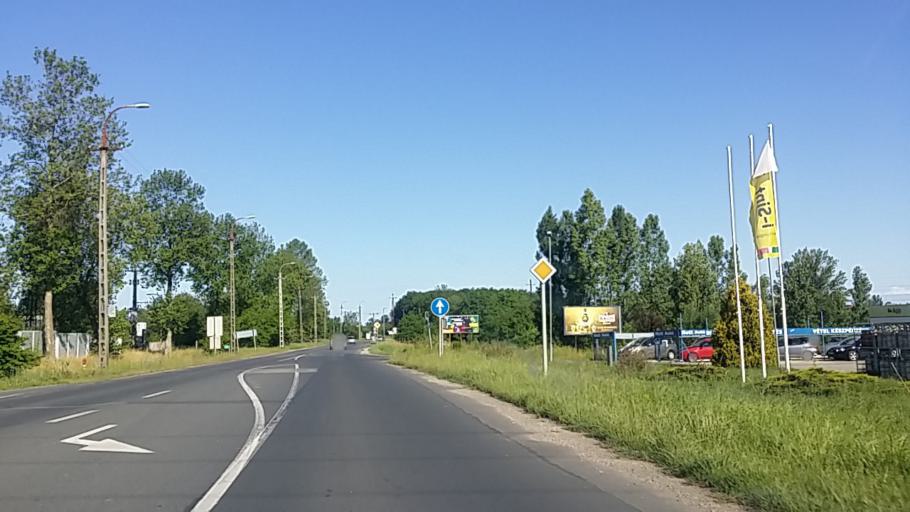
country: HU
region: Zala
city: Zalaegerszeg
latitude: 46.8557
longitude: 16.8049
